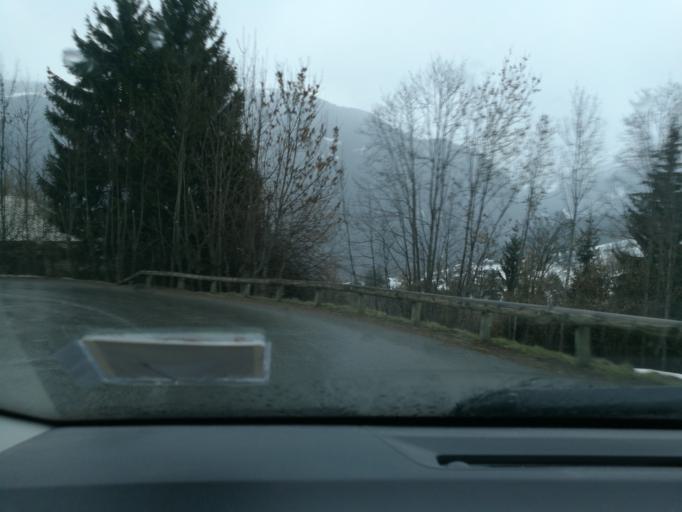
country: FR
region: Rhone-Alpes
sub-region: Departement de la Haute-Savoie
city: Saint-Gervais-les-Bains
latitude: 45.8737
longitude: 6.7020
